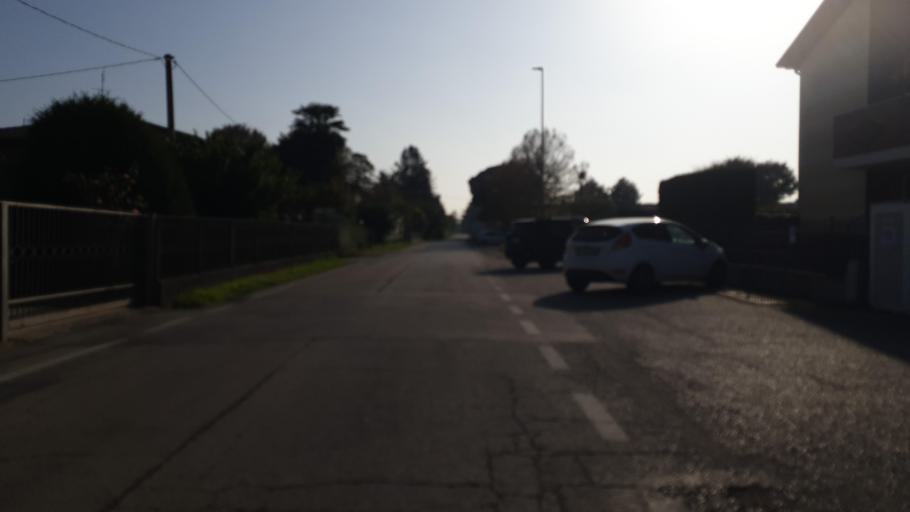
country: IT
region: Veneto
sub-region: Provincia di Padova
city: Oltre Brenta
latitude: 45.4039
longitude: 11.9980
